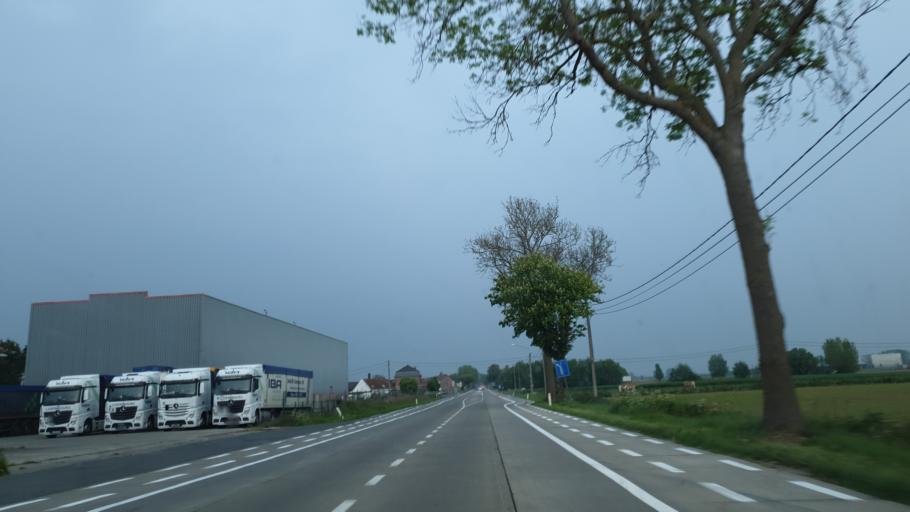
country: BE
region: Flanders
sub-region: Provincie West-Vlaanderen
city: Poperinge
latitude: 50.9207
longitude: 2.7556
